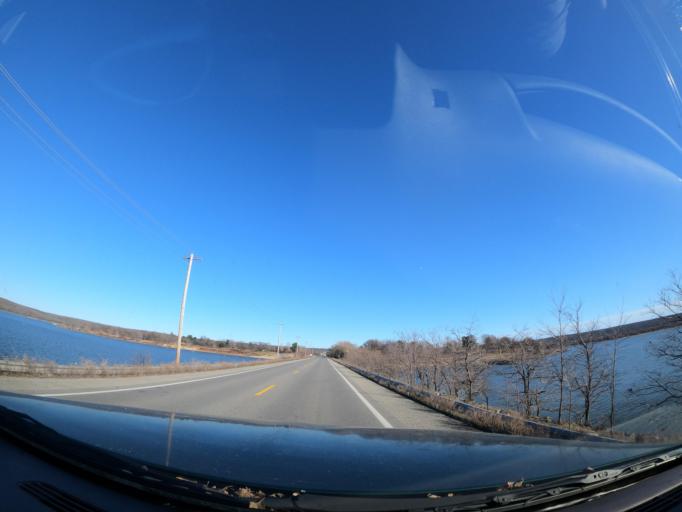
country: US
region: Oklahoma
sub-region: Pittsburg County
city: Longtown
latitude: 35.2392
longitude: -95.4985
